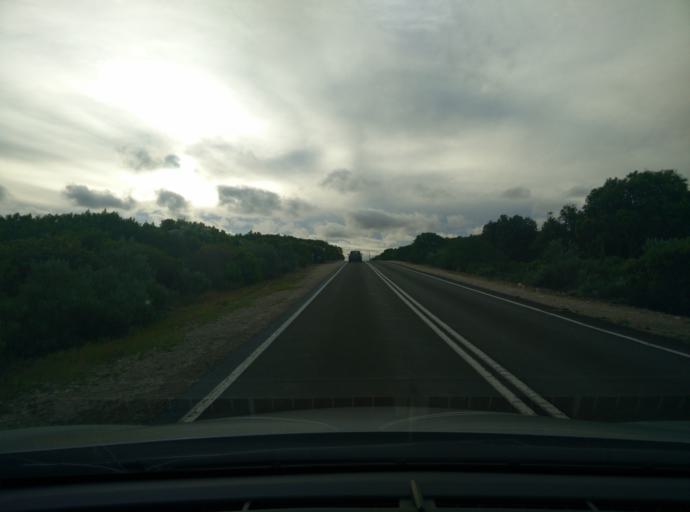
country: AU
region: South Australia
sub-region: Kangaroo Island
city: Kingscote
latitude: -35.8358
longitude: 137.7925
